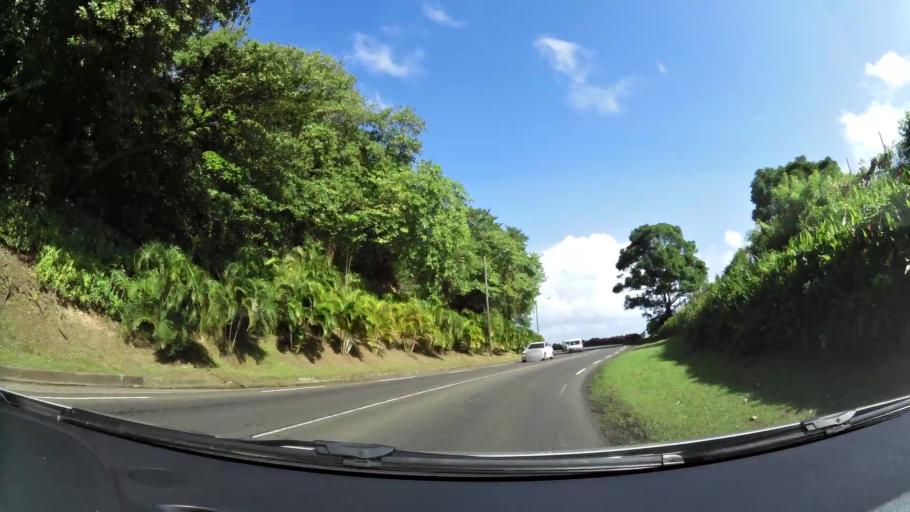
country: MQ
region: Martinique
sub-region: Martinique
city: Sainte-Marie
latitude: 14.7741
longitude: -60.9905
